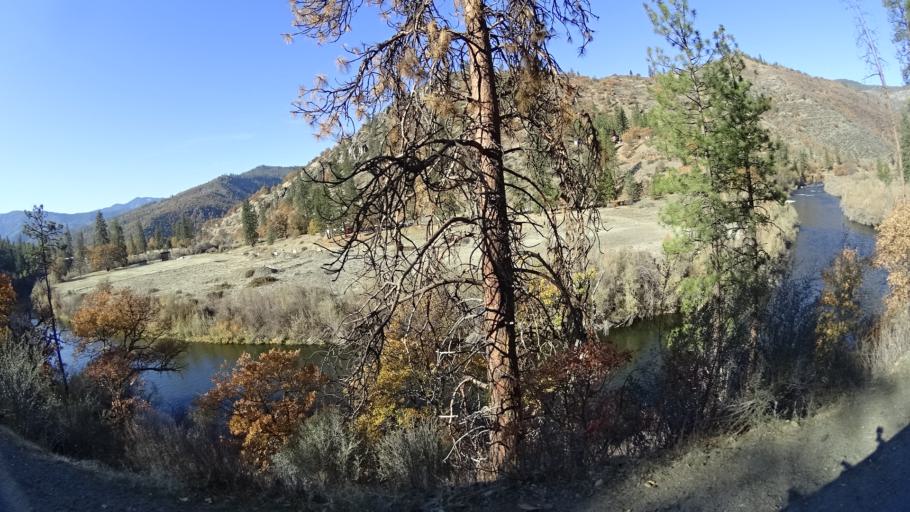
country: US
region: California
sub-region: Siskiyou County
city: Yreka
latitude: 41.8388
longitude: -122.8357
